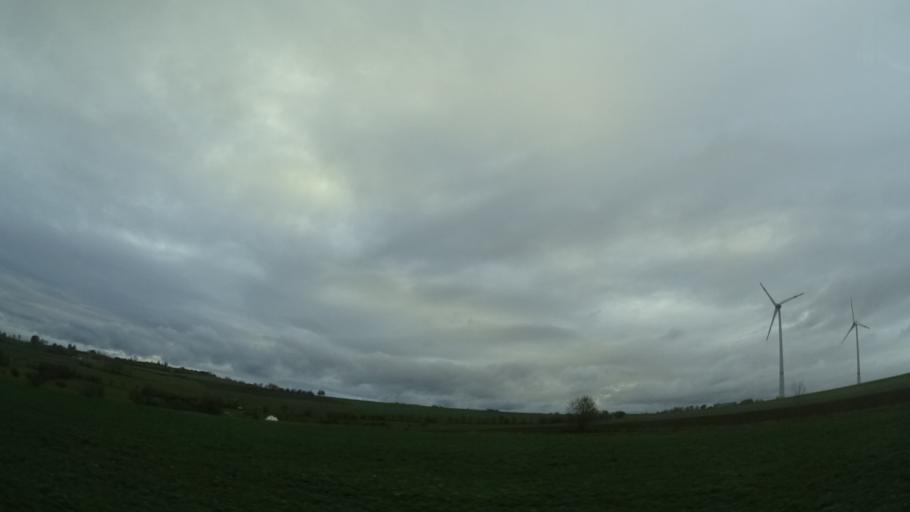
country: DE
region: Hesse
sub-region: Regierungsbezirk Giessen
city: Freiensteinau
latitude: 50.4356
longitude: 9.4010
